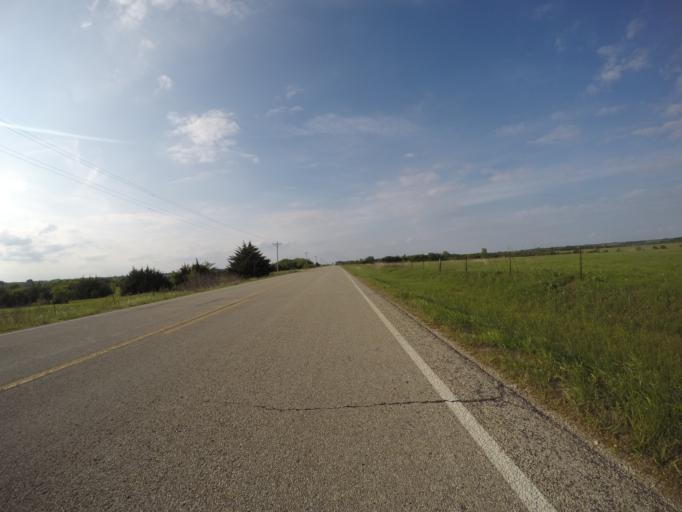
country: US
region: Kansas
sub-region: Pottawatomie County
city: Westmoreland
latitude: 39.4119
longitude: -96.6070
